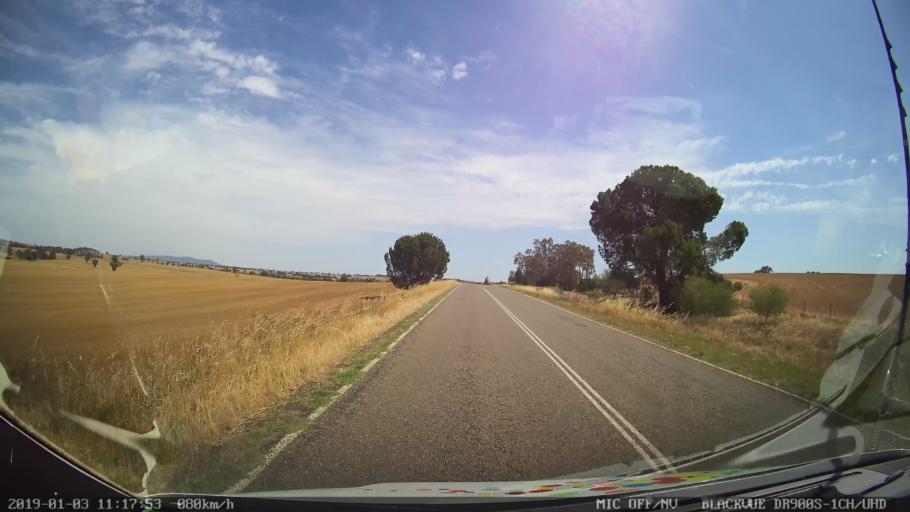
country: AU
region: New South Wales
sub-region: Young
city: Young
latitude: -34.1331
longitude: 148.2642
